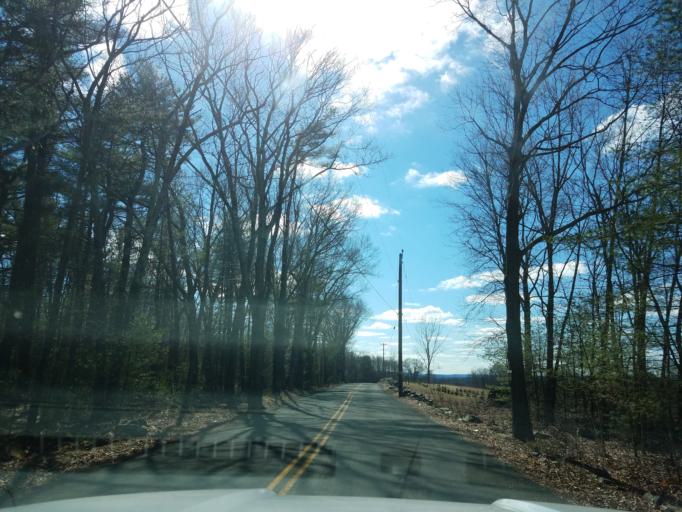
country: US
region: Connecticut
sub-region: Windham County
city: North Grosvenor Dale
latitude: 41.9827
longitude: -71.8749
